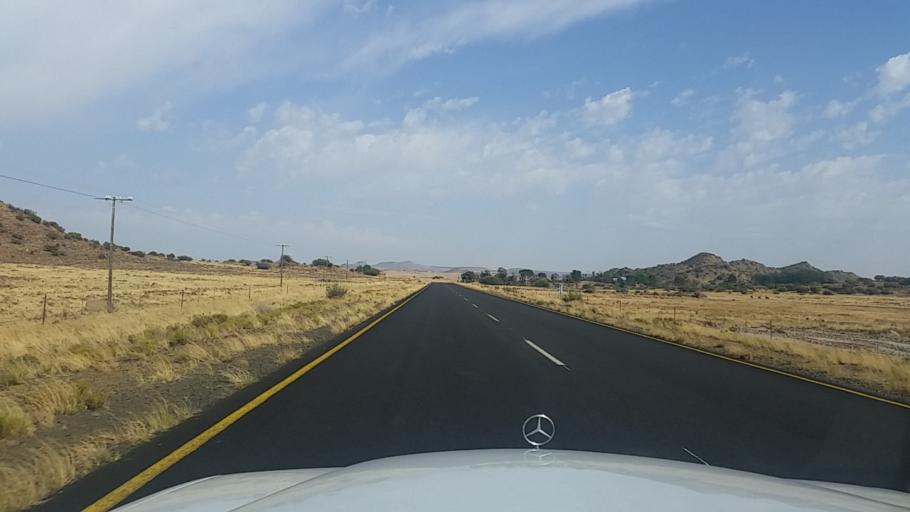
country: ZA
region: Orange Free State
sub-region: Xhariep District Municipality
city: Trompsburg
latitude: -30.3177
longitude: 25.7597
